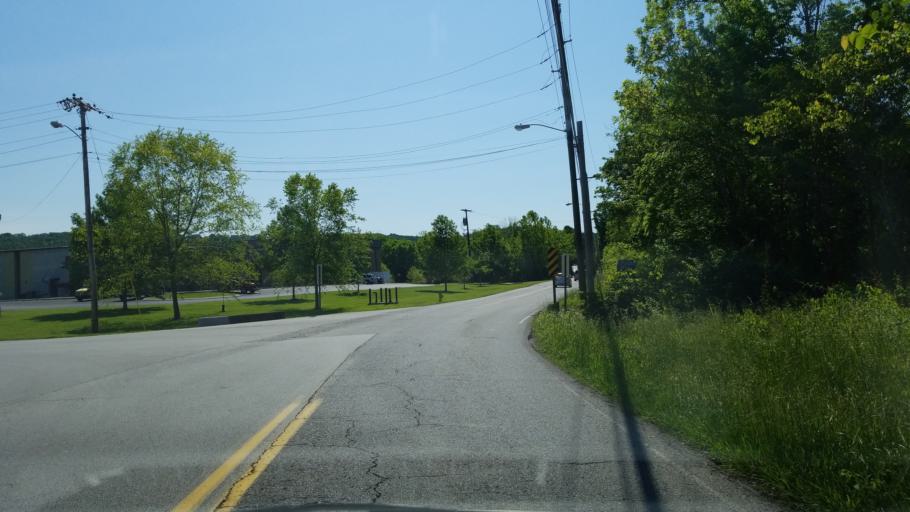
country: US
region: Tennessee
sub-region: Hamilton County
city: East Brainerd
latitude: 35.0522
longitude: -85.1389
